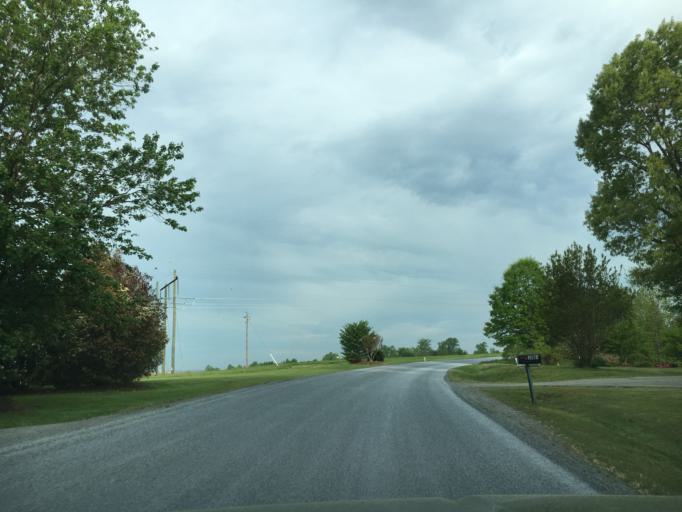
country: US
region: Virginia
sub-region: Campbell County
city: Brookneal
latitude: 36.9476
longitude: -78.9664
